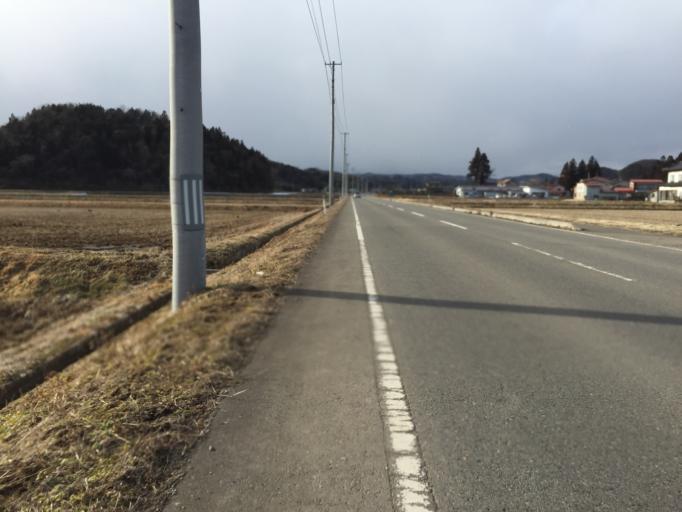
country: JP
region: Tochigi
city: Kuroiso
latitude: 37.1516
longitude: 140.1680
